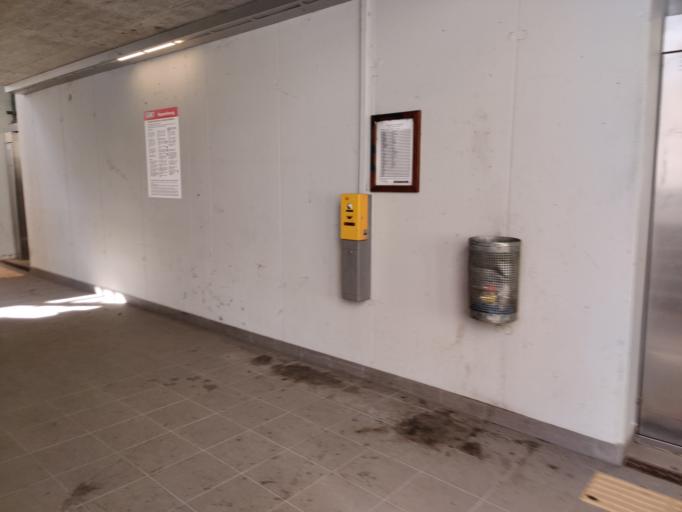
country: AT
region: Styria
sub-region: Politischer Bezirk Voitsberg
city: Voitsberg
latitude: 47.0433
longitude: 15.1503
